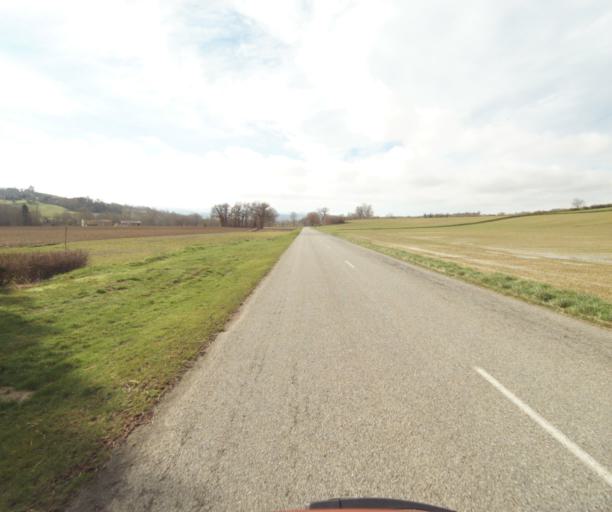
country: FR
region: Midi-Pyrenees
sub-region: Departement de l'Ariege
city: Pamiers
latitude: 43.1362
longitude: 1.5602
